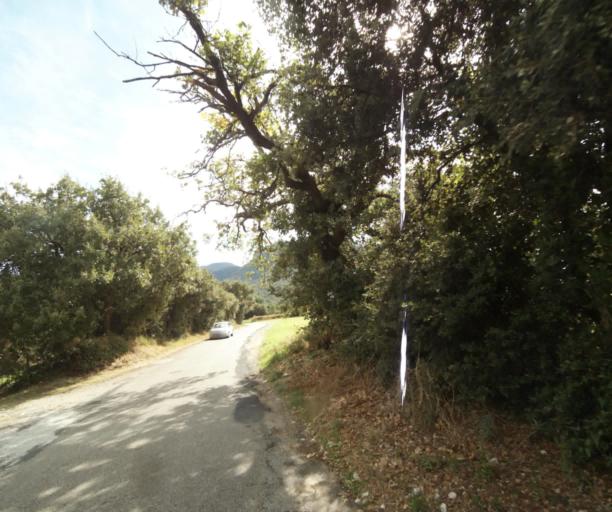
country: FR
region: Languedoc-Roussillon
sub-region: Departement des Pyrenees-Orientales
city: Sant Andreu de Sureda
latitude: 42.5340
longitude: 2.9857
